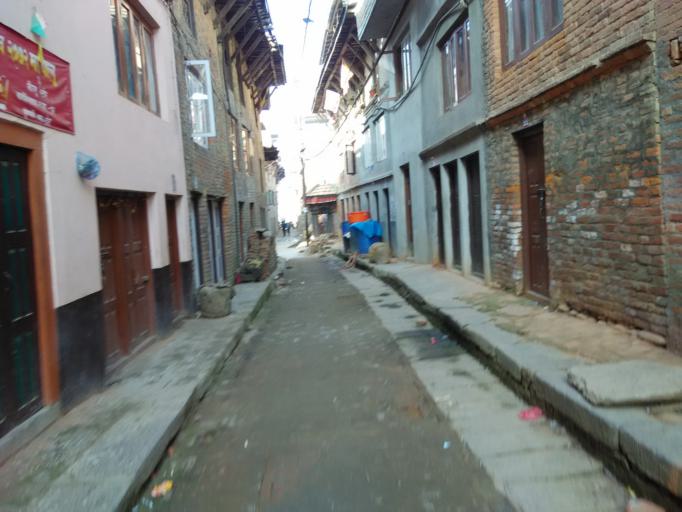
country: NP
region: Central Region
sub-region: Bagmati Zone
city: Patan
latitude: 27.6288
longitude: 85.3027
